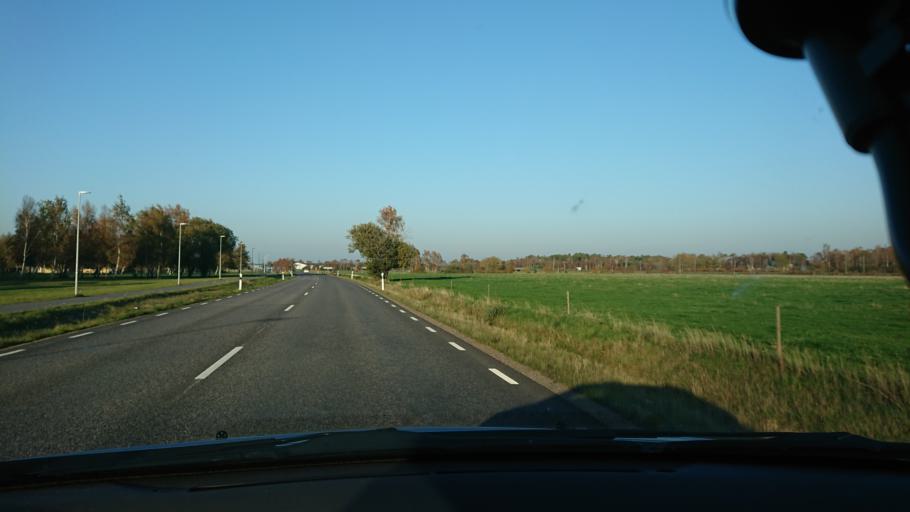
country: SE
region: Halland
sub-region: Laholms Kommun
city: Mellbystrand
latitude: 56.4488
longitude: 12.9326
